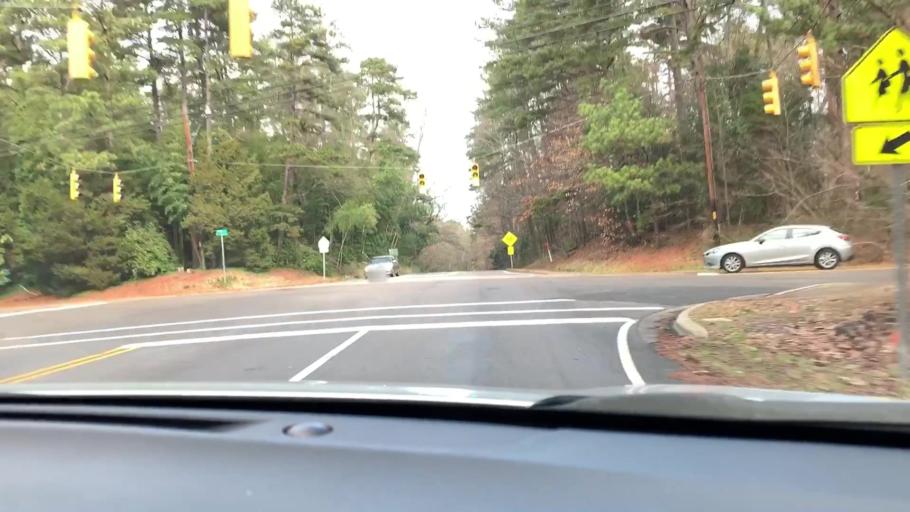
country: US
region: North Carolina
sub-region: Durham County
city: Durham
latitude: 35.9774
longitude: -78.9424
